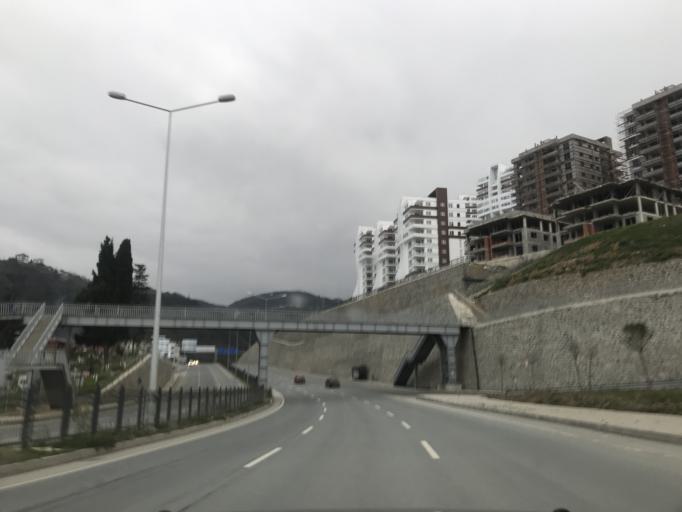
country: TR
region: Trabzon
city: Akcaabat
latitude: 41.0050
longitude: 39.6271
